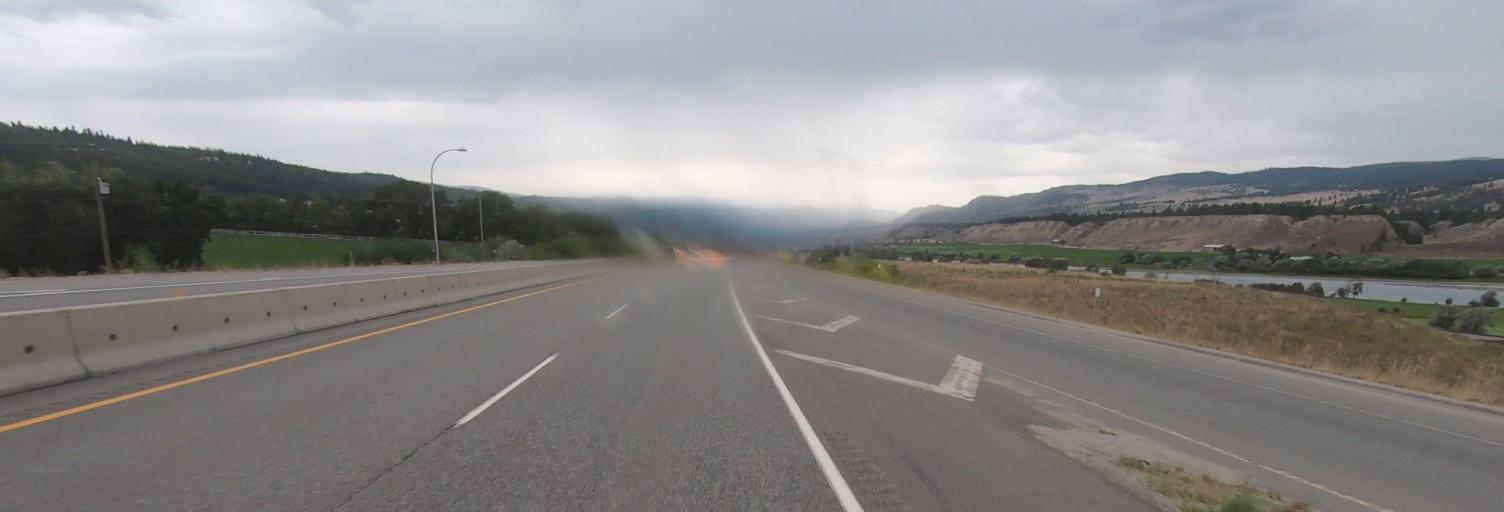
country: CA
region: British Columbia
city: Chase
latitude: 50.6835
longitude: -119.8199
